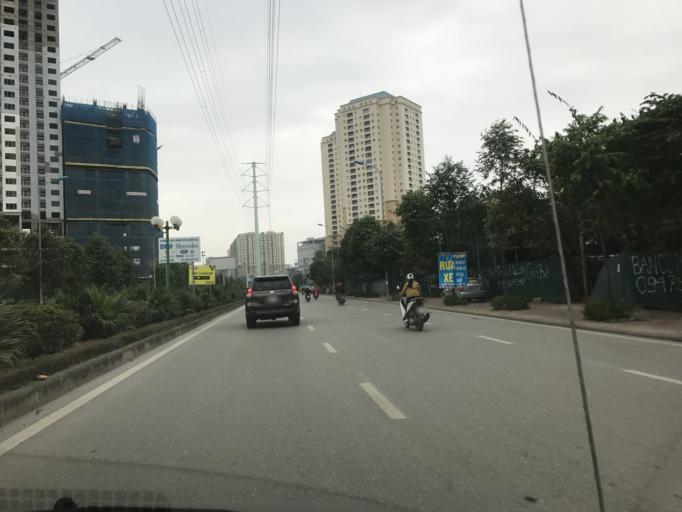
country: VN
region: Ha Noi
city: Thanh Xuan
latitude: 20.9921
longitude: 105.7855
